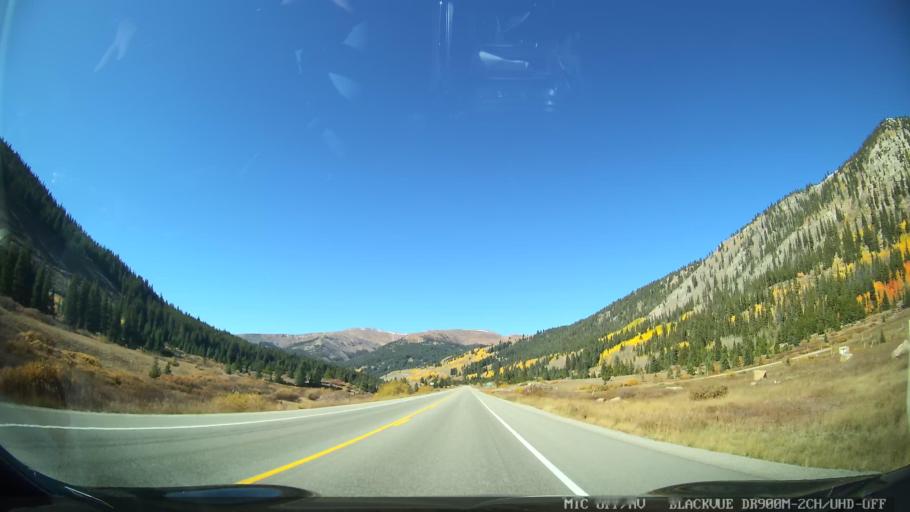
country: US
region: Colorado
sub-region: Lake County
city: Leadville
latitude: 39.3618
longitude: -106.1941
